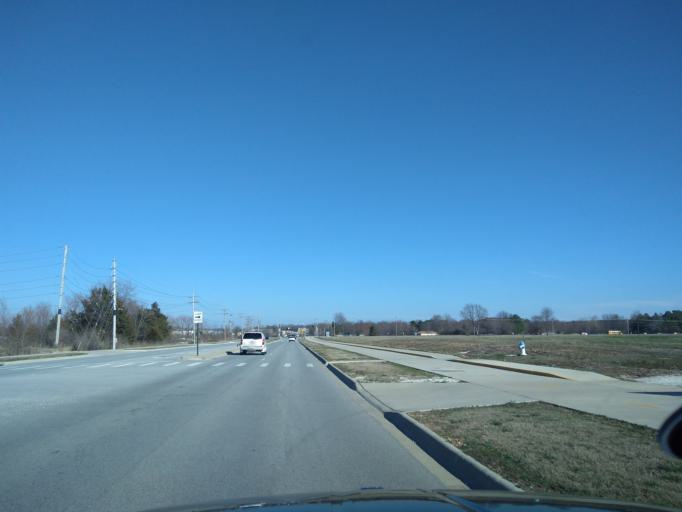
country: US
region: Arkansas
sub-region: Washington County
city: Johnson
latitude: 36.1170
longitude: -94.1674
